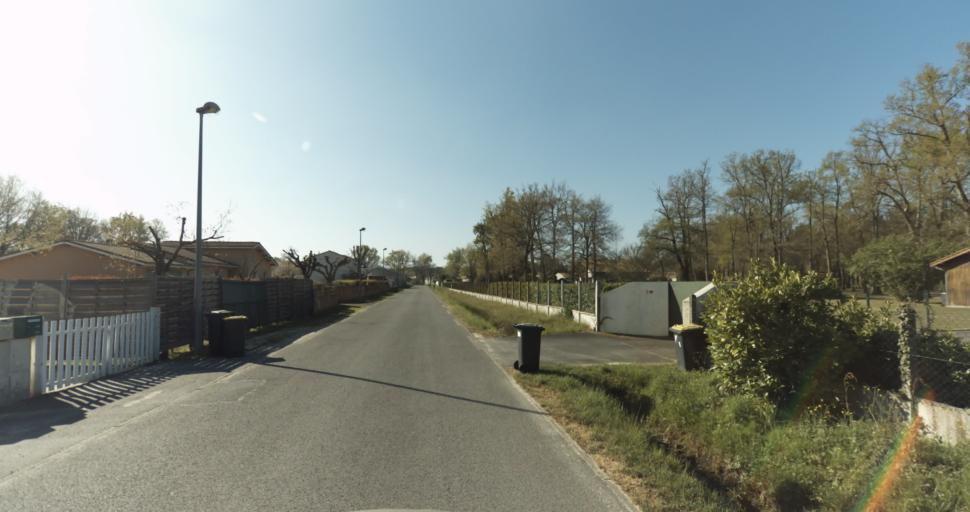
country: FR
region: Aquitaine
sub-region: Departement de la Gironde
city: Martignas-sur-Jalle
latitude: 44.8002
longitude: -0.8382
